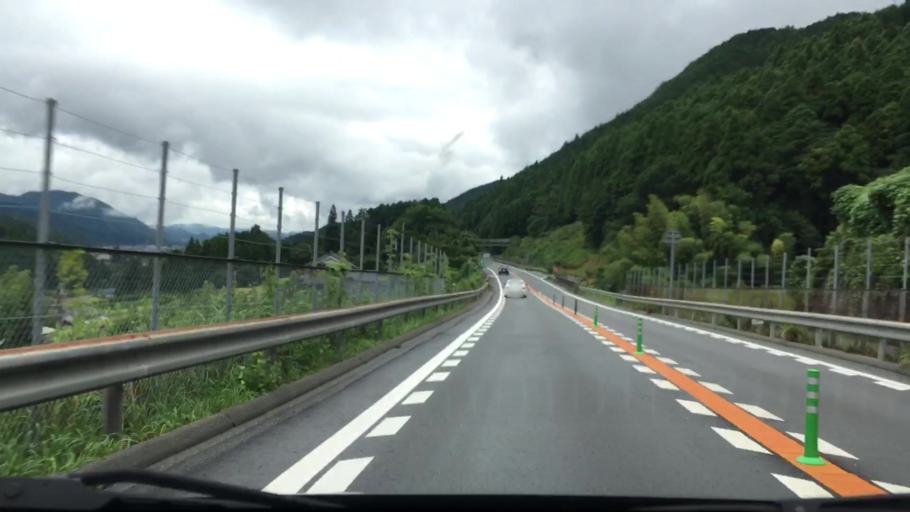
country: JP
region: Hyogo
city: Nishiwaki
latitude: 35.1096
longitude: 134.7807
